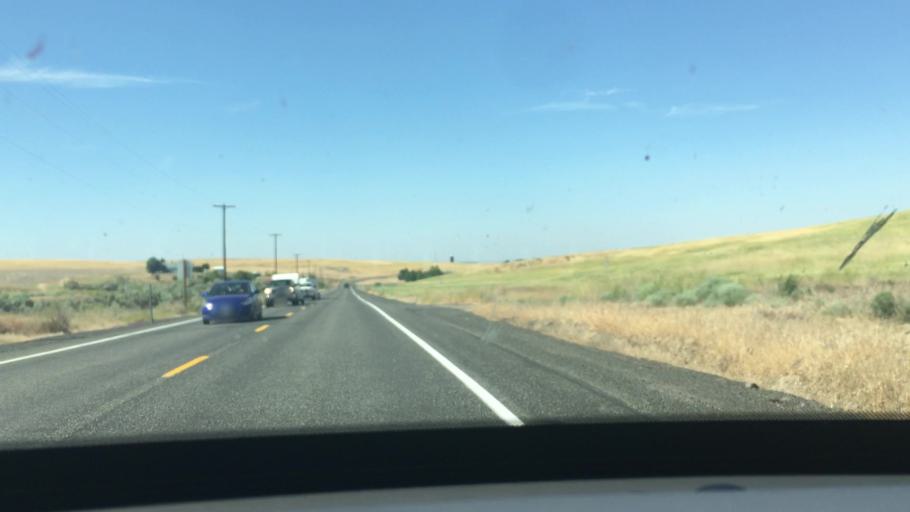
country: US
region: Oregon
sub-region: Sherman County
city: Moro
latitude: 45.4626
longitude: -120.7479
